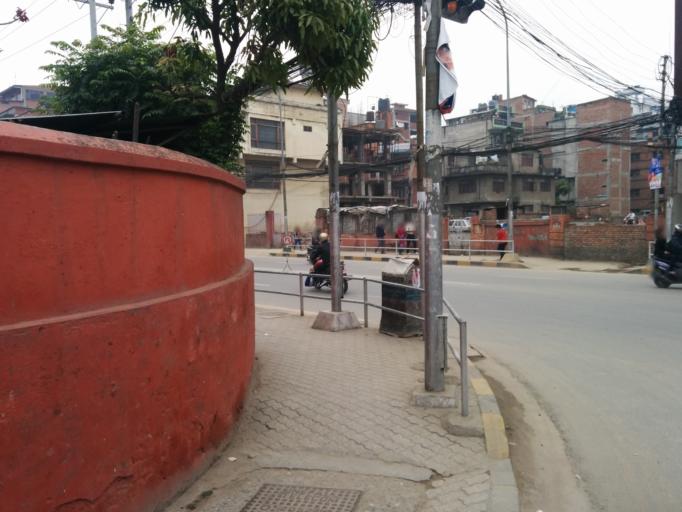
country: NP
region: Central Region
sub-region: Bagmati Zone
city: Kathmandu
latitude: 27.7017
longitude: 85.3221
